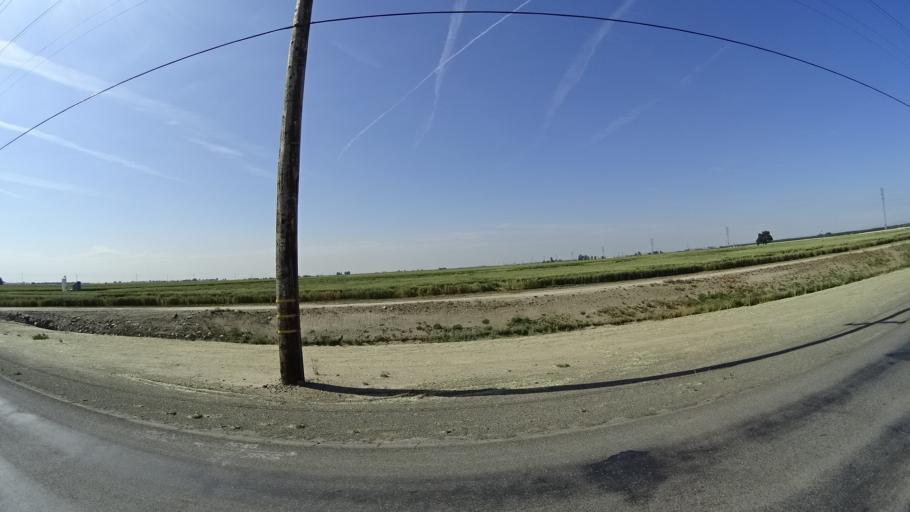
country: US
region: California
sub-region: Kings County
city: Home Garden
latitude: 36.2550
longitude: -119.5885
